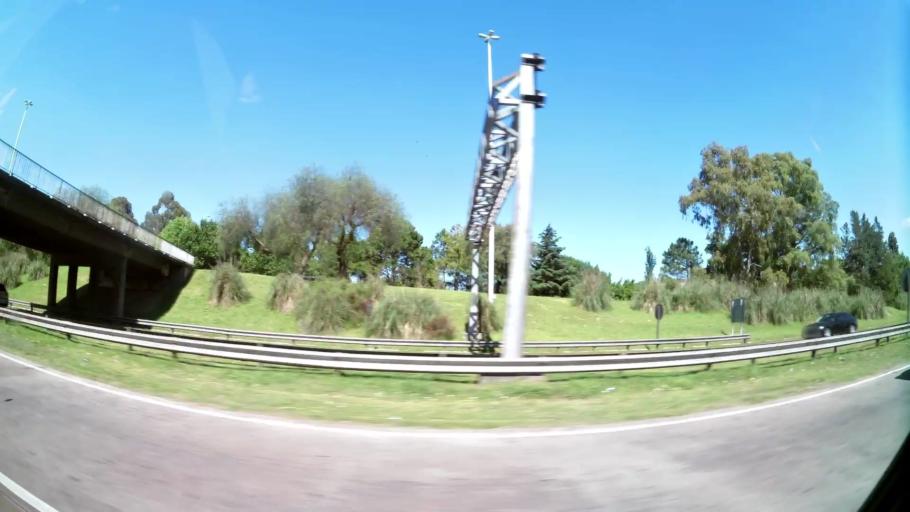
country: AR
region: Buenos Aires
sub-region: Partido de San Isidro
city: San Isidro
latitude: -34.4834
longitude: -58.5607
